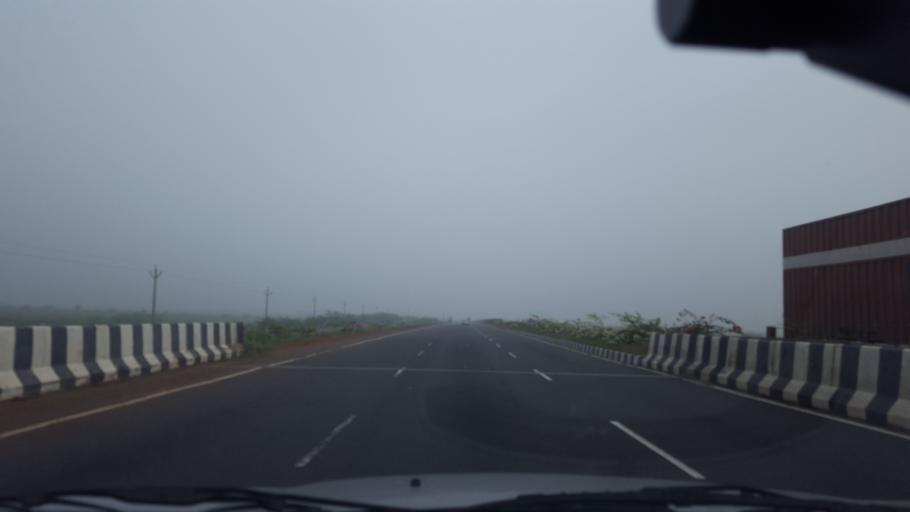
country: IN
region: Andhra Pradesh
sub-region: Prakasam
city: Ongole
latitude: 15.4808
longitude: 80.0608
